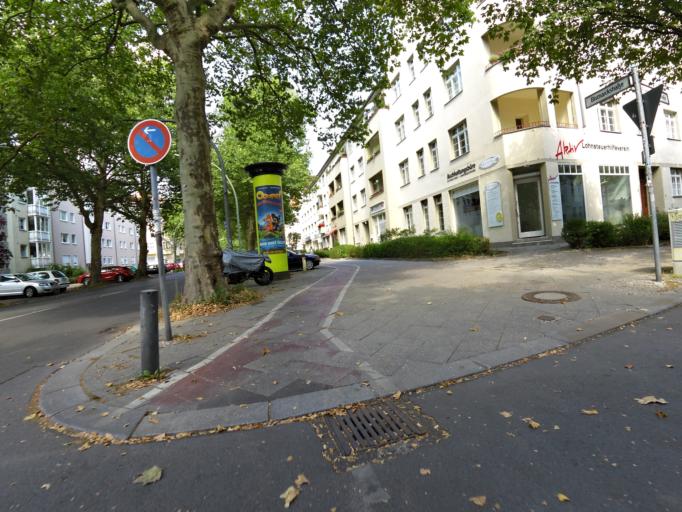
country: DE
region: Berlin
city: Steglitz Bezirk
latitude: 52.4594
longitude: 13.3394
